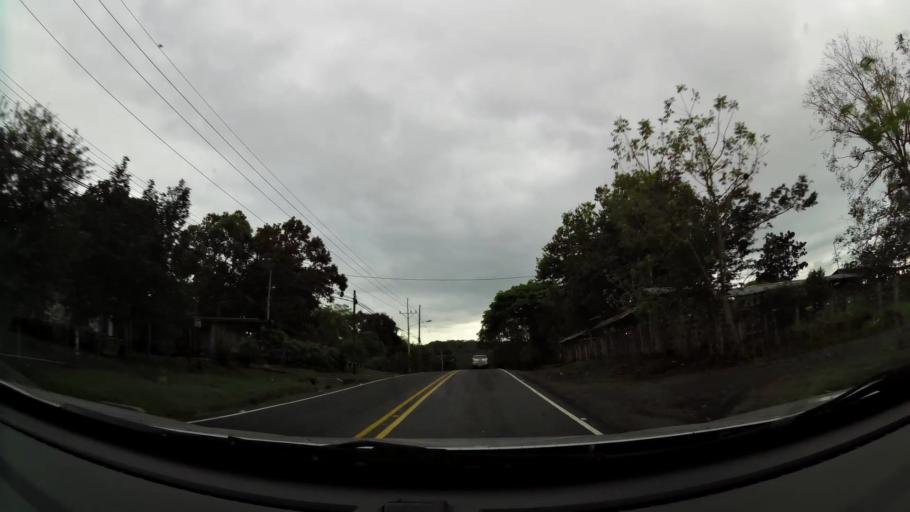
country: CR
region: Alajuela
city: Desamparados
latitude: 9.9396
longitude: -84.5349
